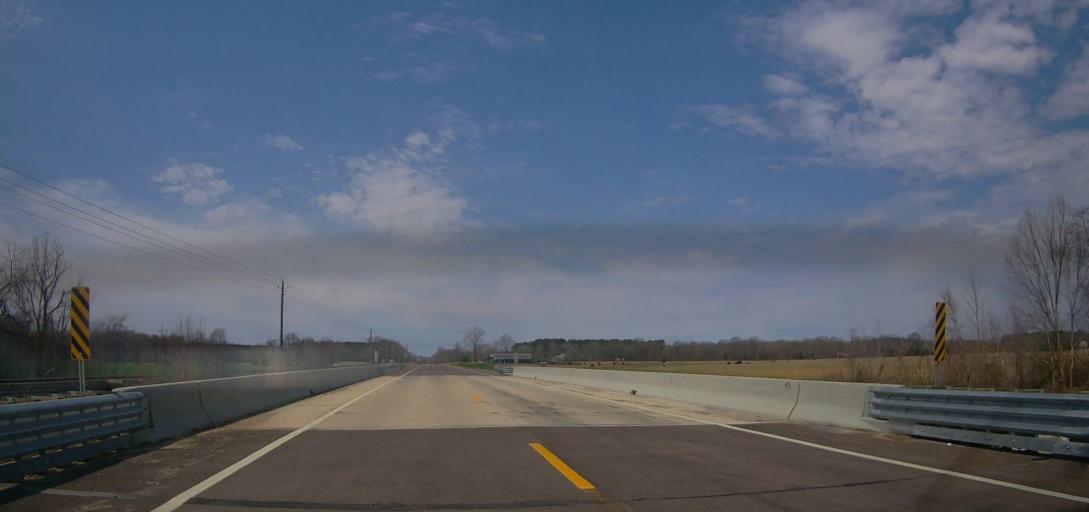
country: US
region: Mississippi
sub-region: Benton County
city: Ashland
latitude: 34.6221
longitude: -89.2372
